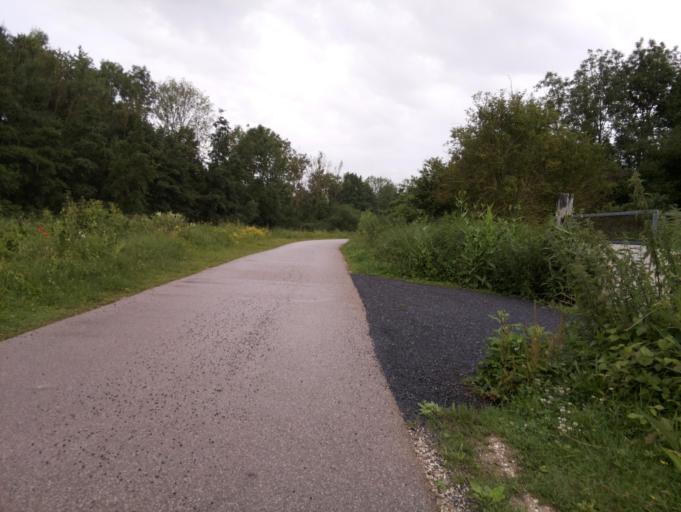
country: FR
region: Picardie
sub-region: Departement de la Somme
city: Ailly-sur-Somme
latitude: 49.9383
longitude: 2.1808
